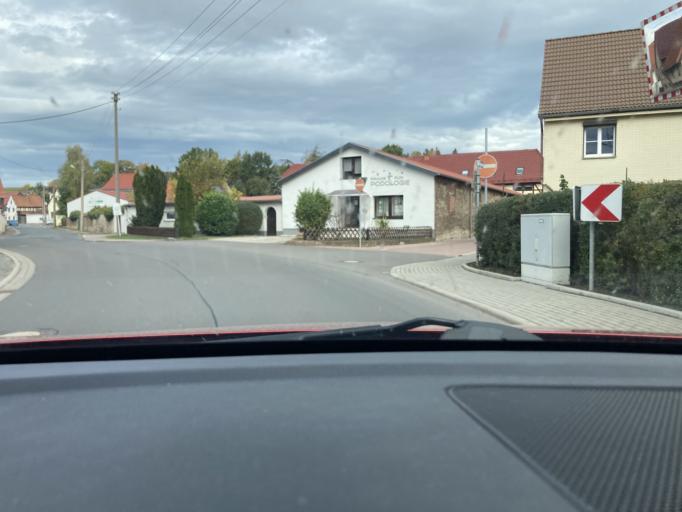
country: DE
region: Thuringia
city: Lipprechterode
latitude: 51.4590
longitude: 10.5569
